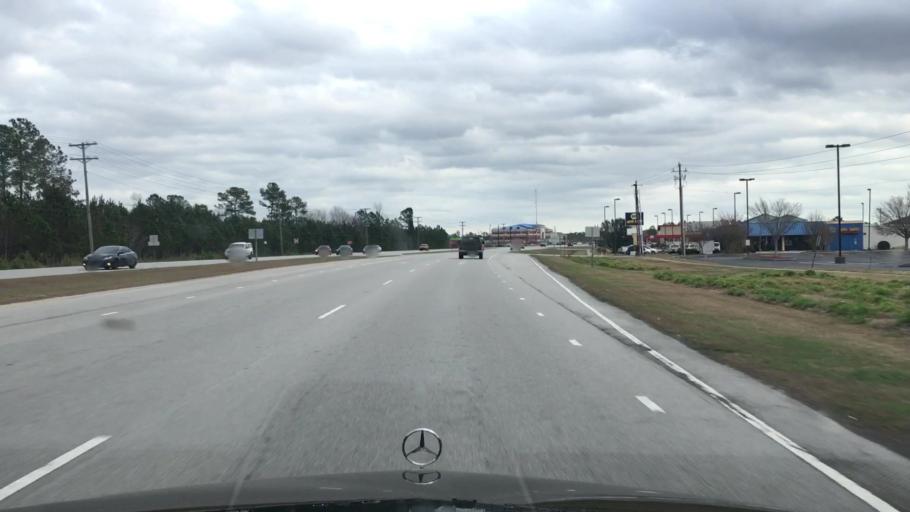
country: US
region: North Carolina
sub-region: Onslow County
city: Half Moon
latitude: 34.8011
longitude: -77.4222
